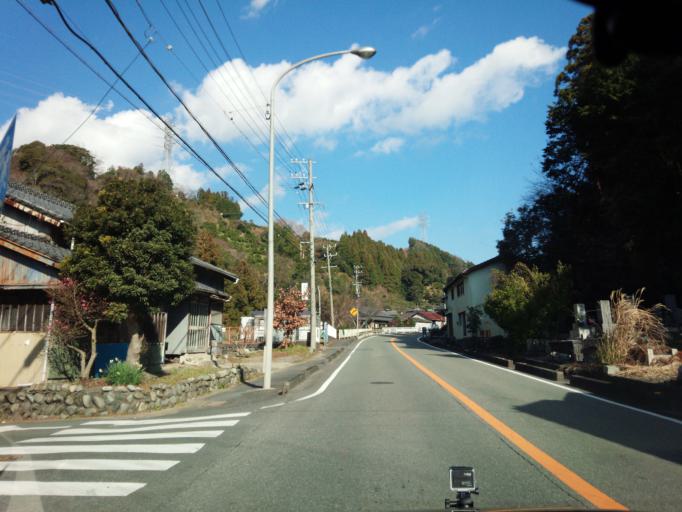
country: JP
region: Shizuoka
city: Fujinomiya
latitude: 35.1250
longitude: 138.5111
